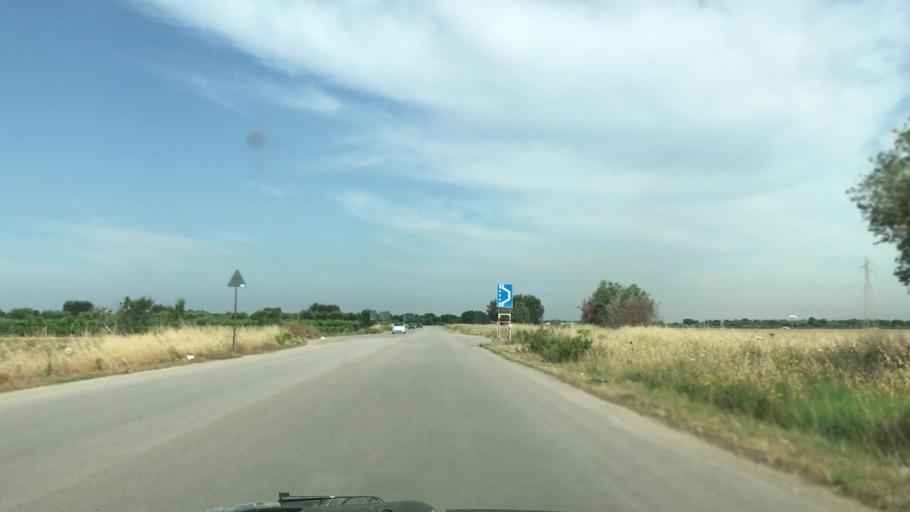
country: IT
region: Apulia
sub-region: Provincia di Taranto
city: San Giorgio Ionico
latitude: 40.4429
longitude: 17.3581
